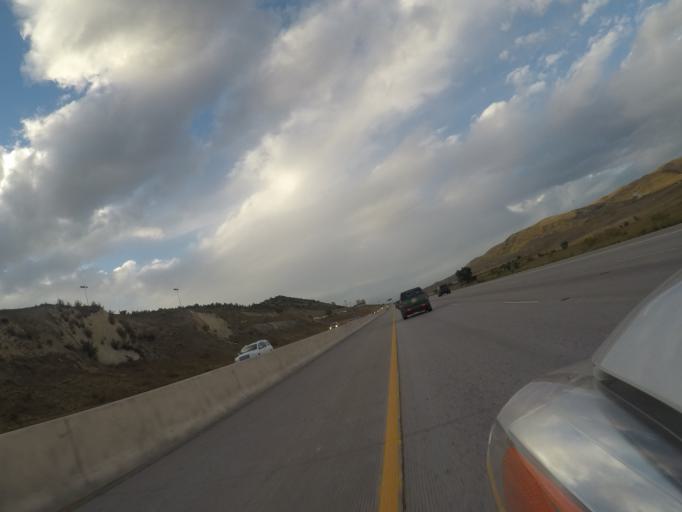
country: US
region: Colorado
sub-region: Jefferson County
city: West Pleasant View
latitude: 39.6685
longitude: -105.1871
